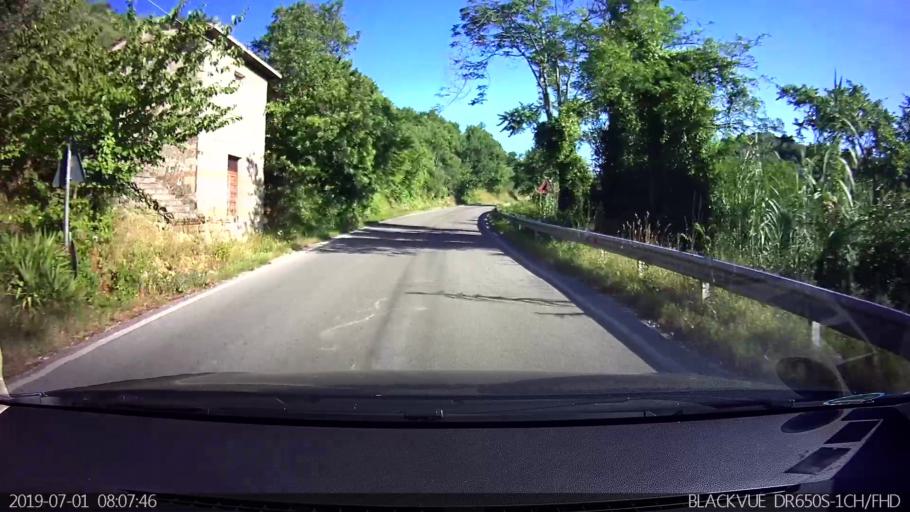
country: IT
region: Latium
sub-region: Provincia di Frosinone
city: Sant'Angelo in Villa-Giglio
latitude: 41.6671
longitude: 13.4233
